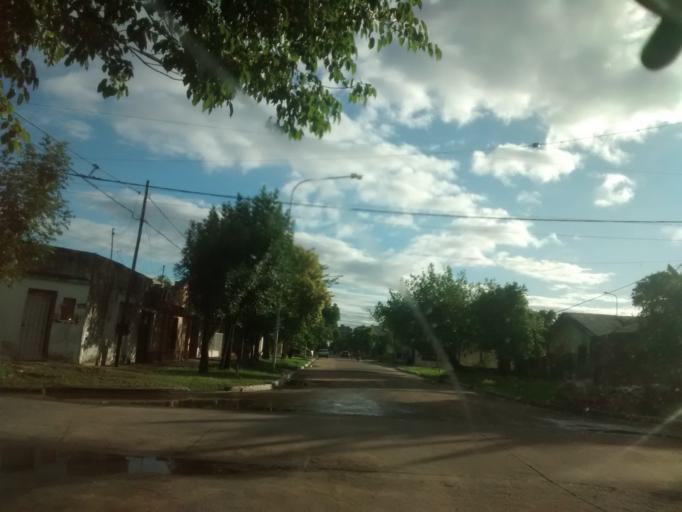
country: AR
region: Chaco
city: Resistencia
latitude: -27.4543
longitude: -59.0023
